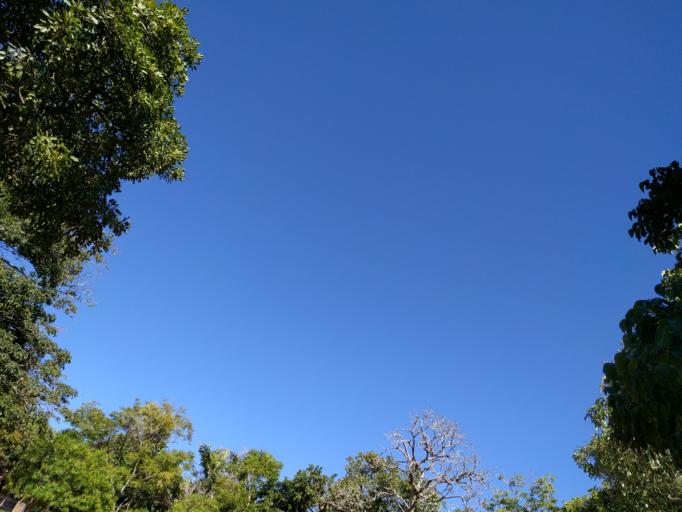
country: BO
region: Santa Cruz
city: Santa Rita
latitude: -17.8918
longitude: -63.3312
